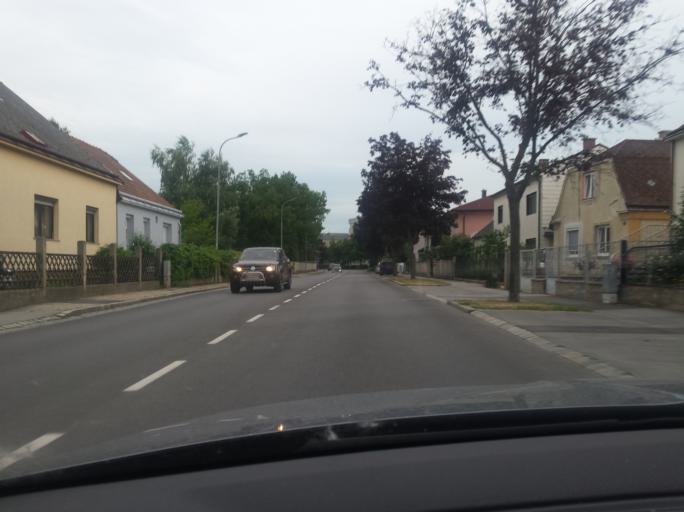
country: AT
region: Lower Austria
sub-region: Politischer Bezirk Ganserndorf
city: Deutsch-Wagram
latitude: 48.3092
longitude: 16.5707
